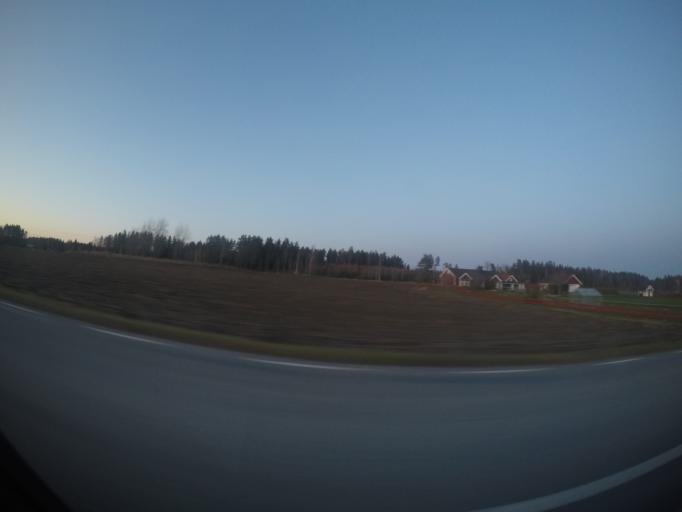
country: SE
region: OErebro
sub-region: Lindesbergs Kommun
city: Frovi
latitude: 59.3262
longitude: 15.4388
